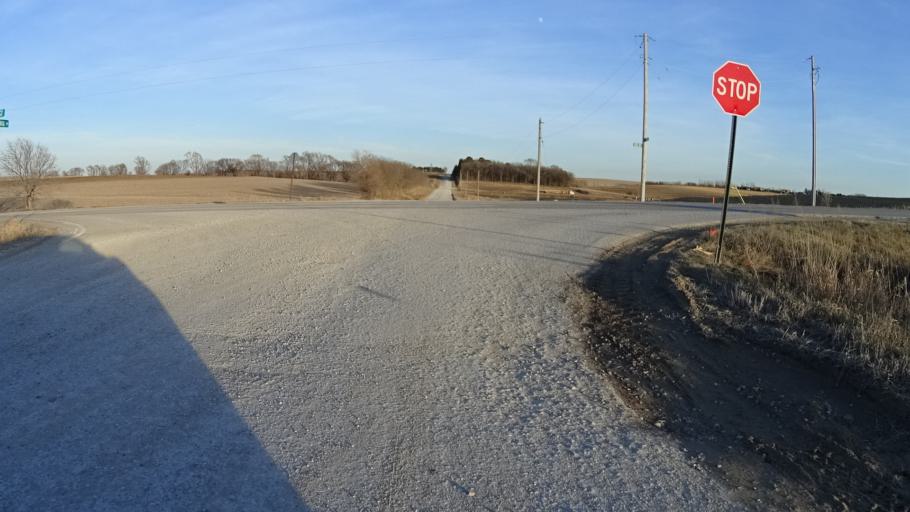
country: US
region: Nebraska
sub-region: Sarpy County
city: Springfield
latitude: 41.1326
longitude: -96.1199
